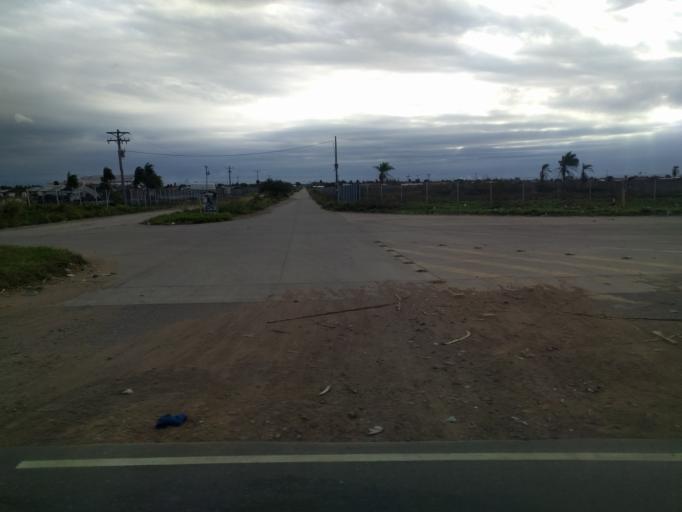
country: BO
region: Santa Cruz
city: La Belgica
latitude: -17.5881
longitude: -63.1582
